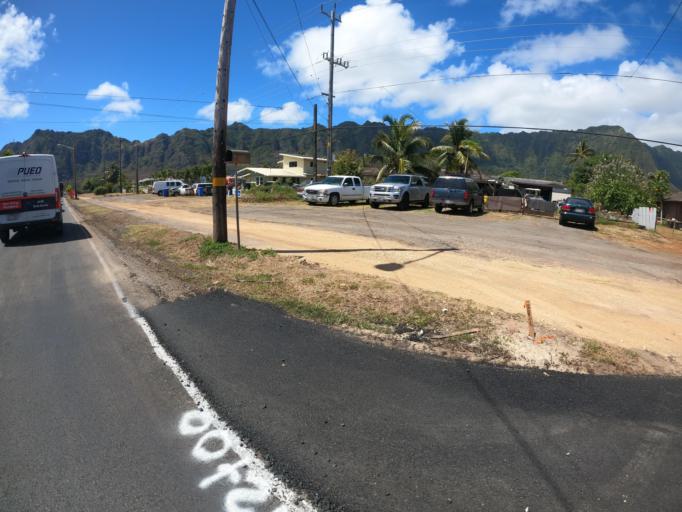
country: US
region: Hawaii
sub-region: Honolulu County
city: Waimanalo Beach
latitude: 21.3373
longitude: -157.7013
